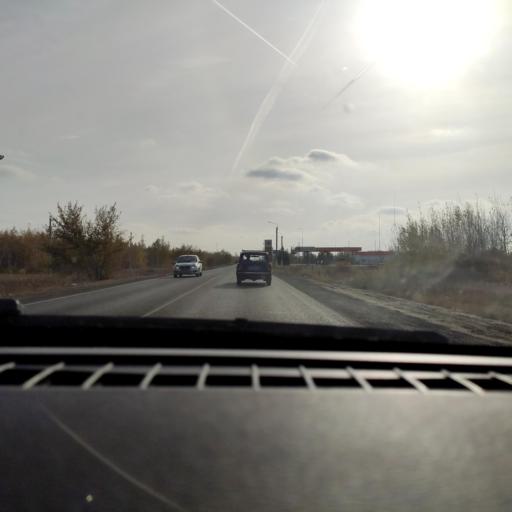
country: RU
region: Voronezj
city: Maslovka
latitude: 51.5879
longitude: 39.2533
